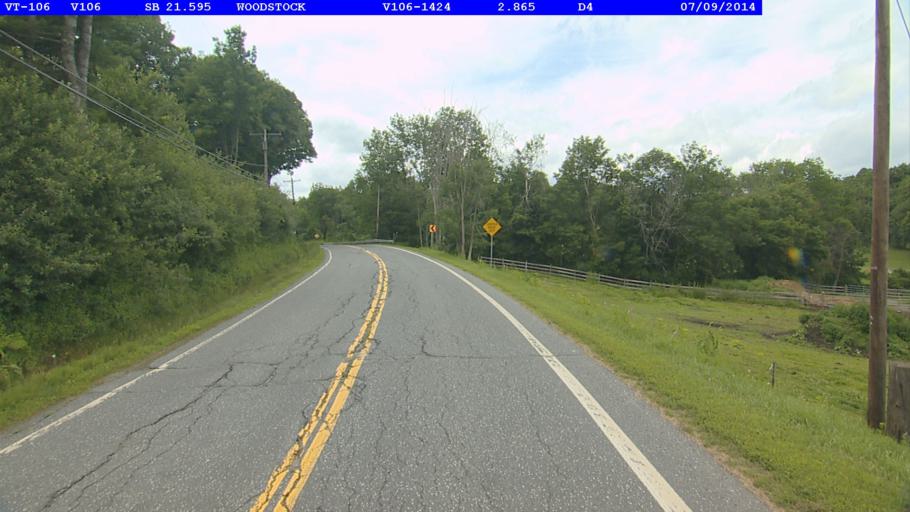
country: US
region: Vermont
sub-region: Windsor County
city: Woodstock
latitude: 43.5665
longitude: -72.5256
